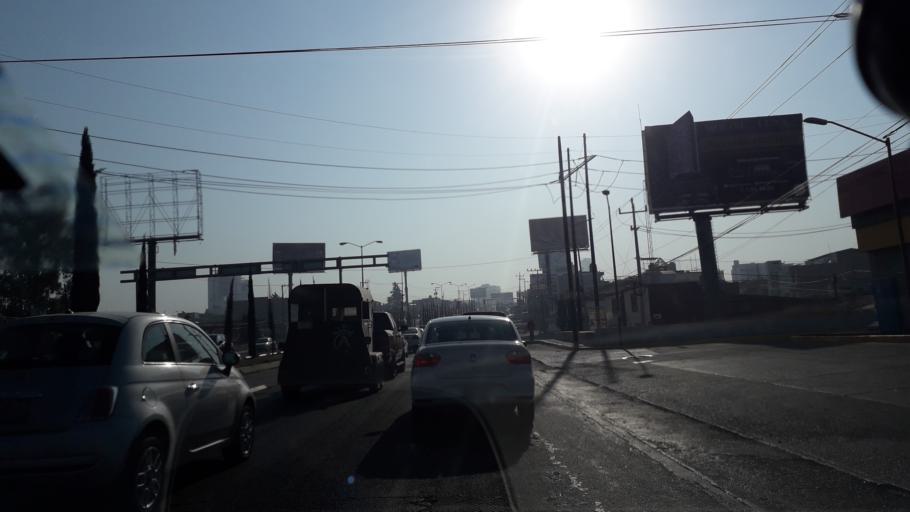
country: MX
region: Puebla
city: Tlazcalancingo
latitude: 19.0359
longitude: -98.2548
